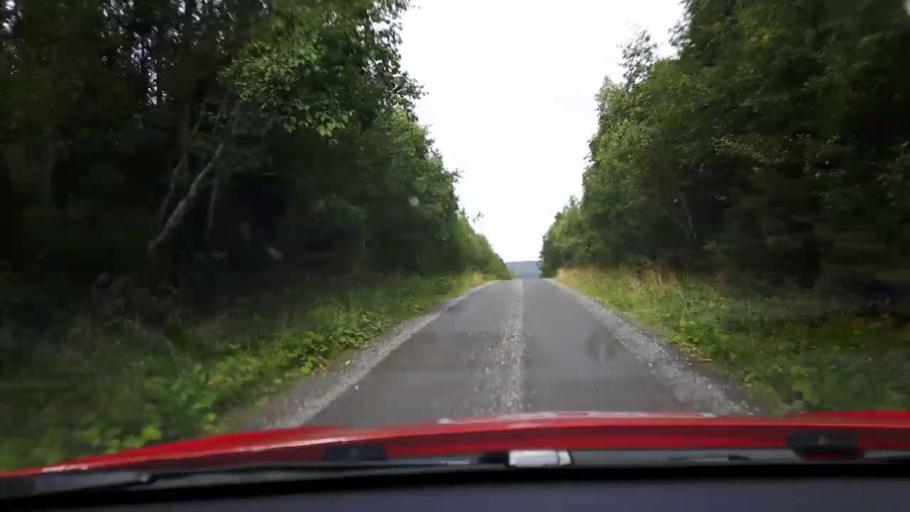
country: SE
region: Jaemtland
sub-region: Are Kommun
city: Are
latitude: 63.7857
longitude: 13.1045
